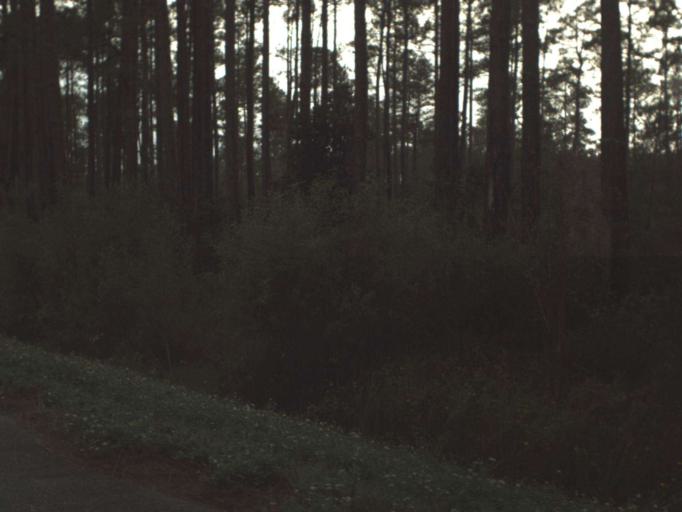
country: US
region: Florida
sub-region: Franklin County
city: Apalachicola
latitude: 29.8762
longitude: -84.9757
